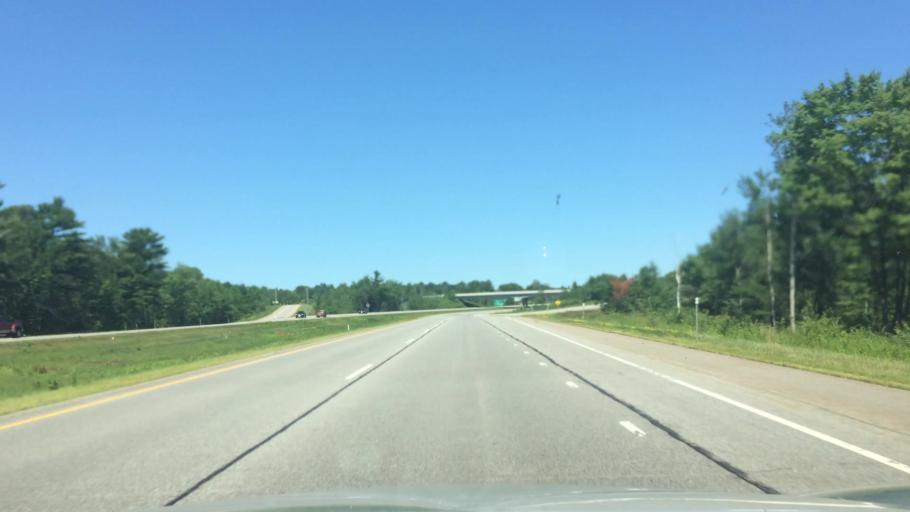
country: US
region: Wisconsin
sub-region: Marathon County
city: Mosinee
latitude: 44.7257
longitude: -89.6745
